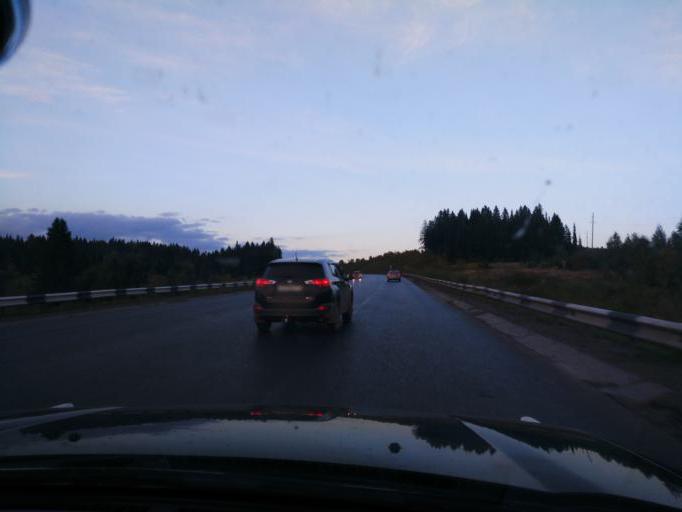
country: RU
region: Perm
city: Polazna
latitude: 58.2840
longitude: 56.4653
